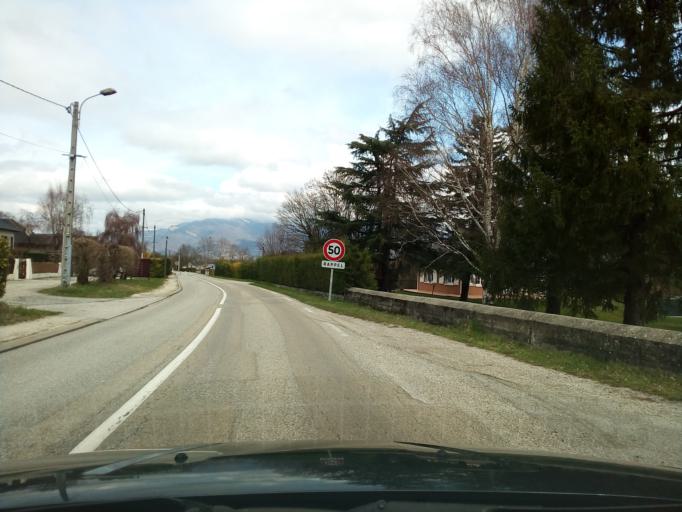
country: FR
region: Rhone-Alpes
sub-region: Departement de la Savoie
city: Saint-Baldoph
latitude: 45.5138
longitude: 5.9588
